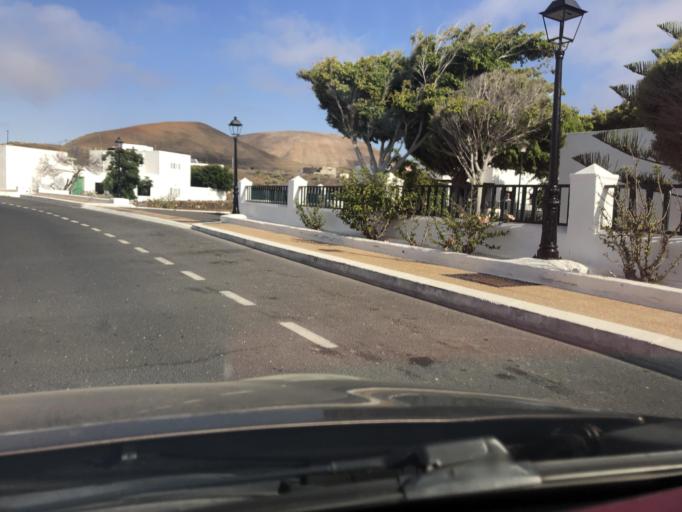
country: ES
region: Canary Islands
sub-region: Provincia de Las Palmas
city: Yaiza
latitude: 28.9525
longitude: -13.7631
